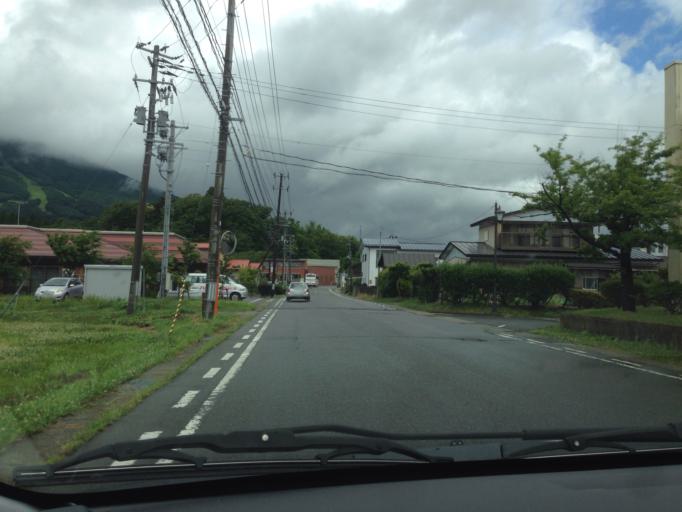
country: JP
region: Fukushima
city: Inawashiro
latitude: 37.5587
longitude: 140.1043
